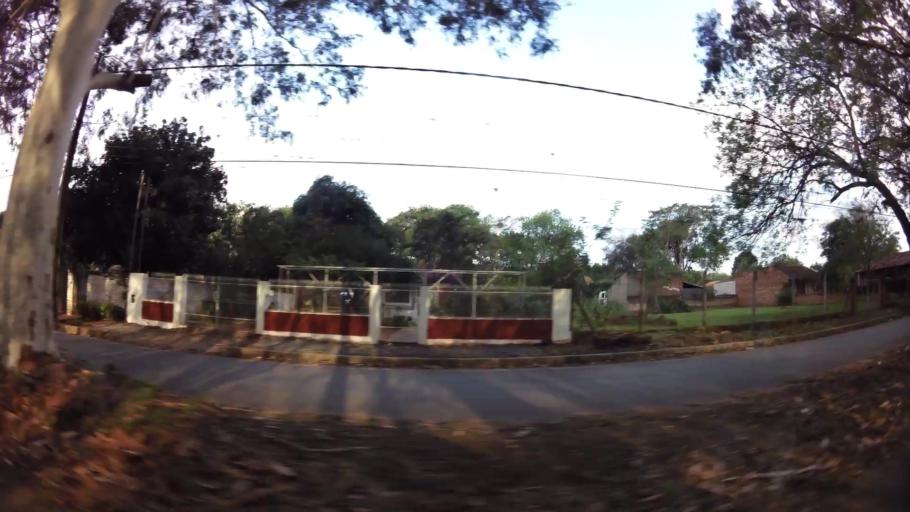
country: PY
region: Central
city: Fernando de la Mora
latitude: -25.3610
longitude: -57.5226
